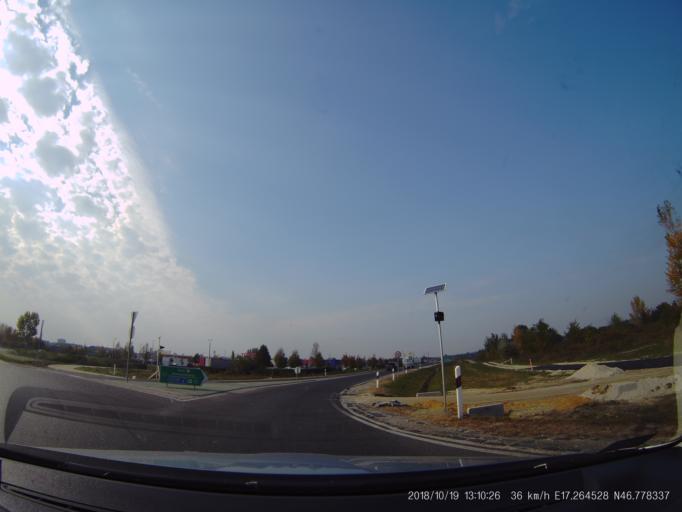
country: HU
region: Zala
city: Gyenesdias
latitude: 46.7784
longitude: 17.2645
